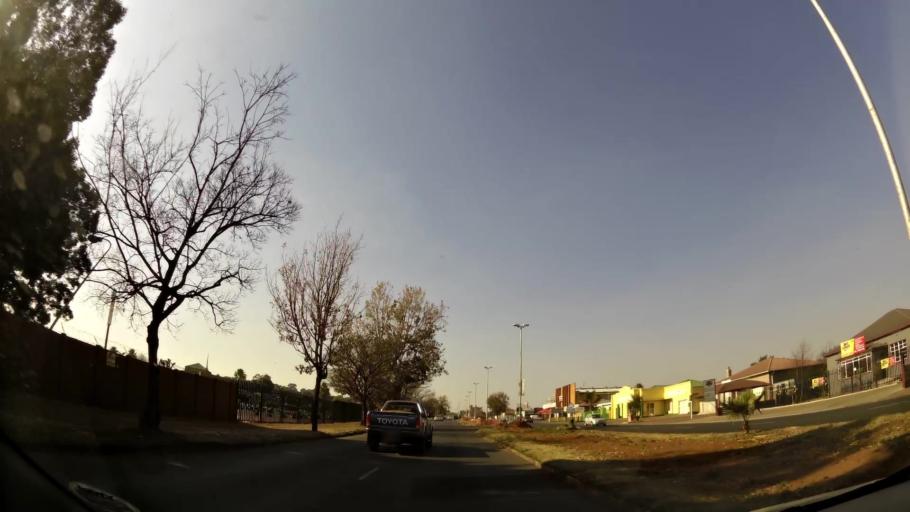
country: ZA
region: Gauteng
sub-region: West Rand District Municipality
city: Randfontein
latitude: -26.1711
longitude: 27.6995
